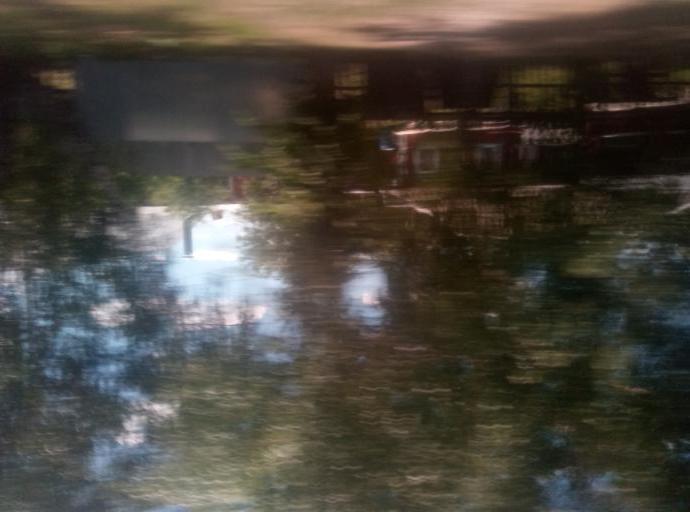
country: RU
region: Tula
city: Kireyevsk
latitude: 53.9716
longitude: 37.9301
